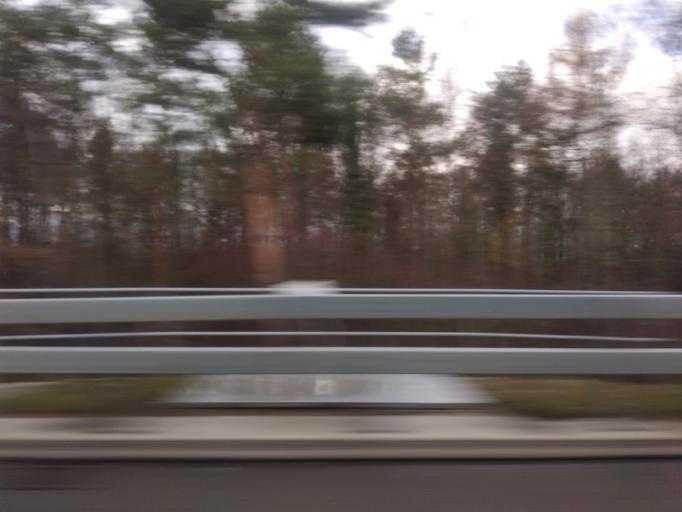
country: CH
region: Zurich
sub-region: Bezirk Winterthur
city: Sulz
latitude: 47.5324
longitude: 8.7980
